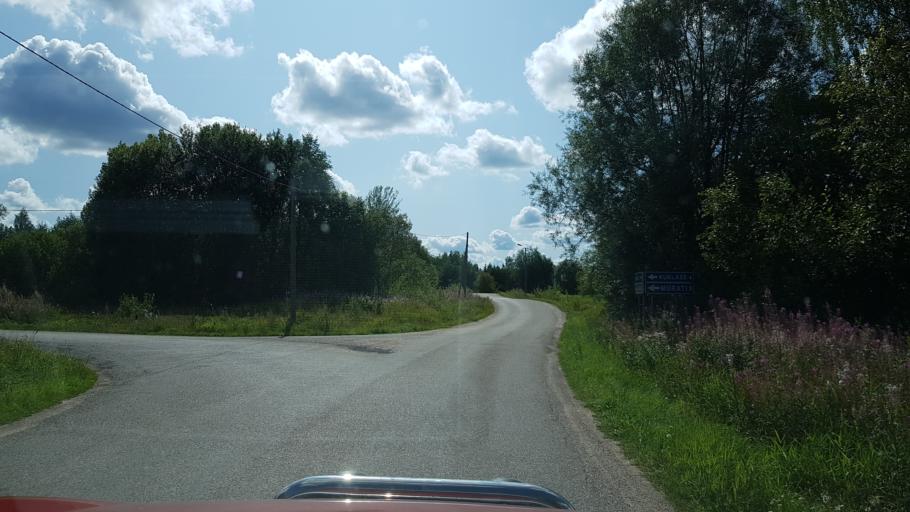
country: EE
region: Vorumaa
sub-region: Voru linn
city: Voru
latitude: 57.6326
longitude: 27.0900
